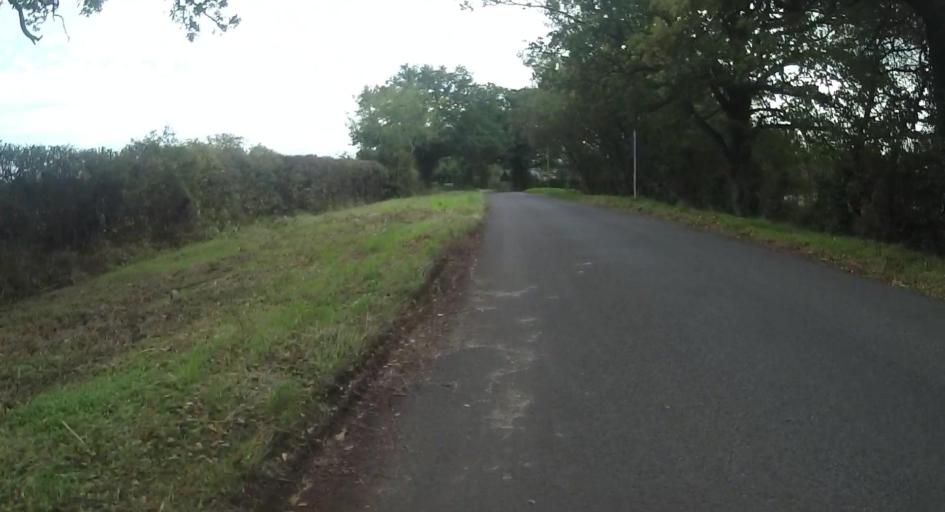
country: GB
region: England
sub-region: Hampshire
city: Fleet
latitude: 51.2849
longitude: -0.8897
